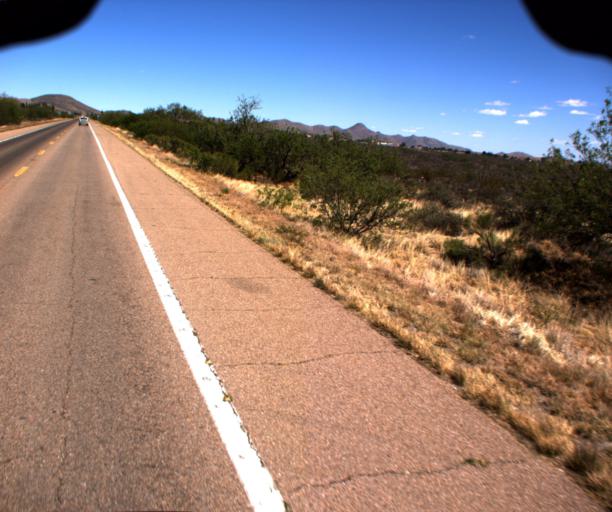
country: US
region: Arizona
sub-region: Cochise County
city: Naco
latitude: 31.3889
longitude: -109.9440
